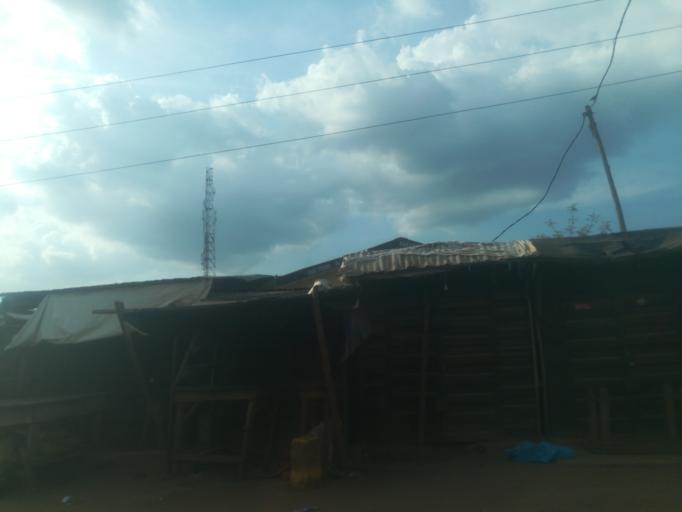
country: NG
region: Ogun
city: Abeokuta
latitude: 7.1199
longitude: 3.3196
